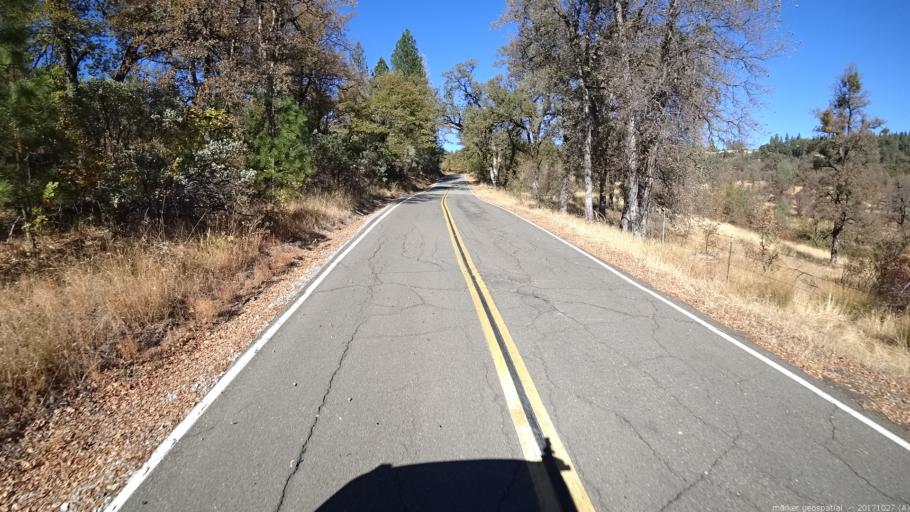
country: US
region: California
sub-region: Shasta County
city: Bella Vista
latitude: 40.7472
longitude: -121.9942
